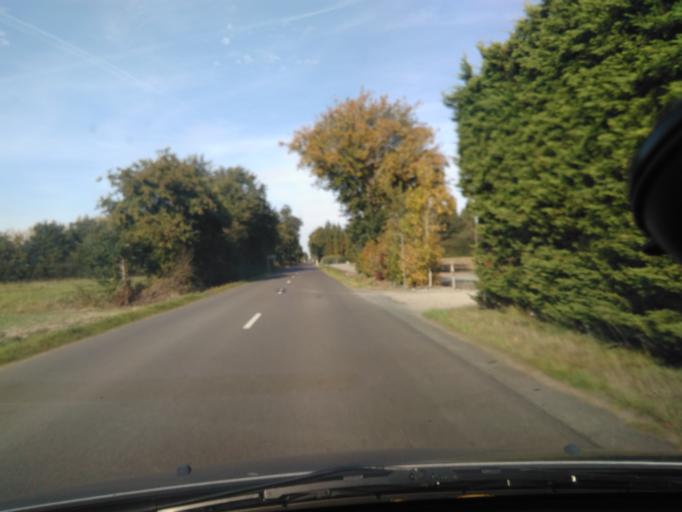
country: FR
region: Pays de la Loire
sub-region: Departement de la Vendee
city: Nieul-le-Dolent
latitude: 46.5305
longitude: -1.5466
